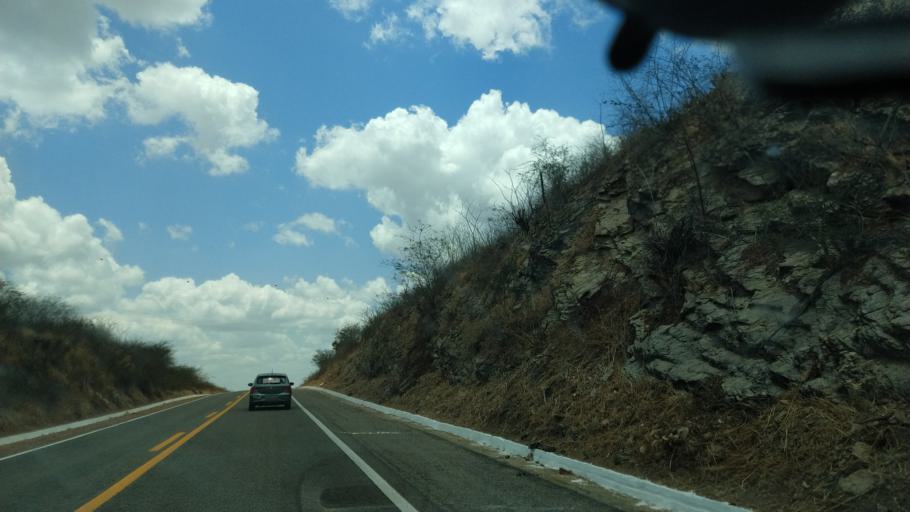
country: BR
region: Rio Grande do Norte
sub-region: Cerro Cora
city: Cerro Cora
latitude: -6.1883
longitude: -36.2431
